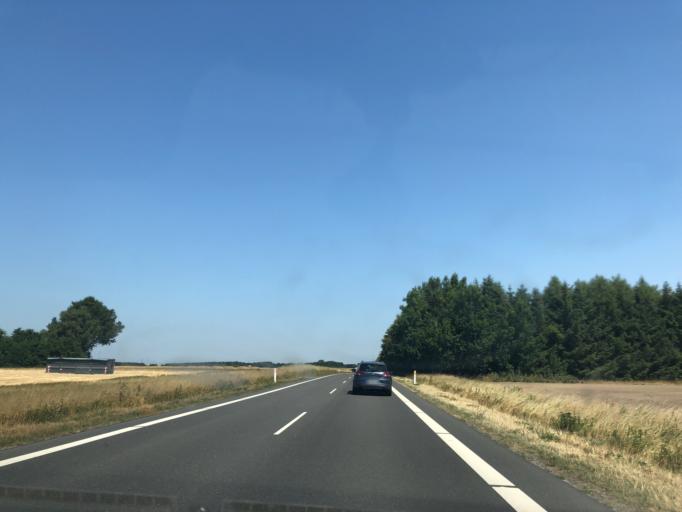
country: DK
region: Zealand
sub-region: Slagelse Kommune
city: Skaelskor
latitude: 55.2405
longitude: 11.3172
